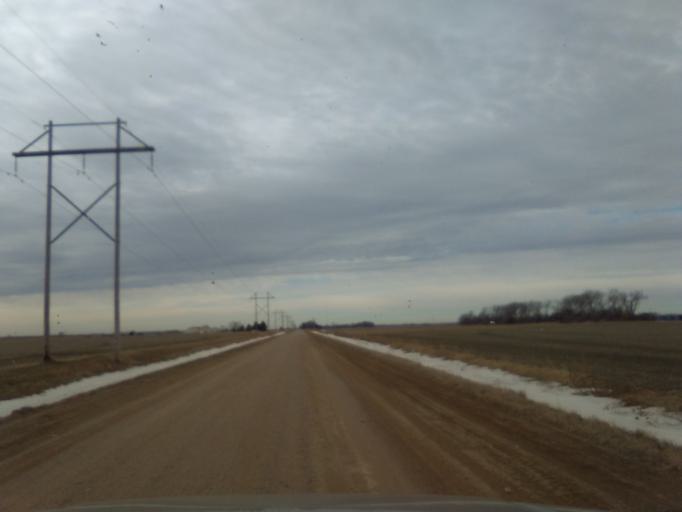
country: US
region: Nebraska
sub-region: Buffalo County
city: Gibbon
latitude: 40.6549
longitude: -98.7860
